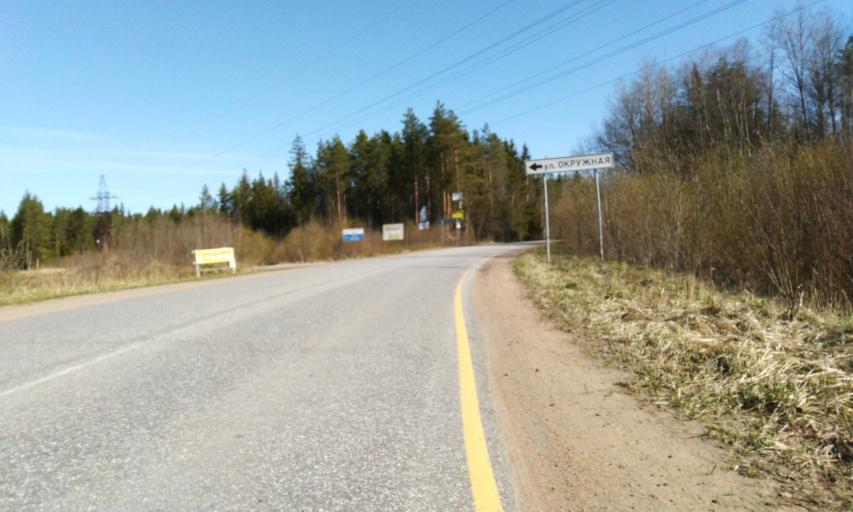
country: RU
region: Leningrad
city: Garbolovo
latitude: 60.3403
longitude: 30.4357
